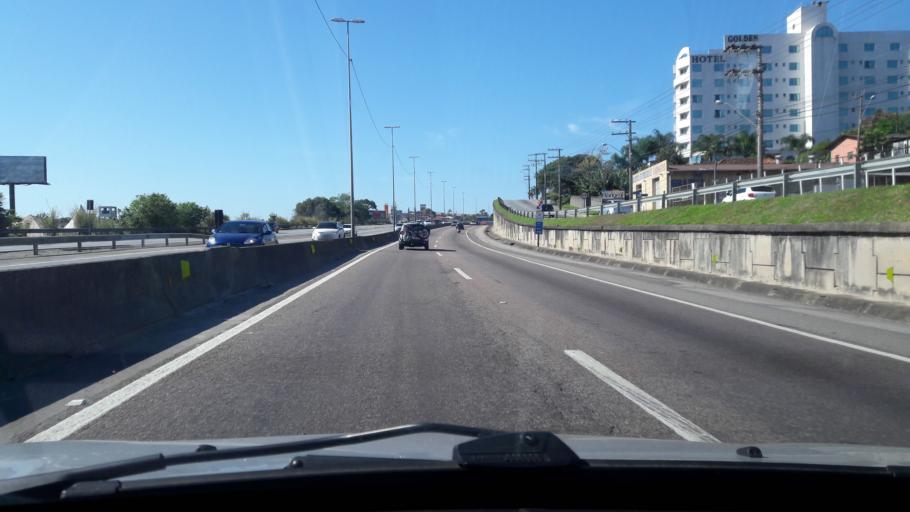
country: BR
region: Santa Catarina
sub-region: Biguacu
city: Biguacu
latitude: -27.5397
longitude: -48.6233
